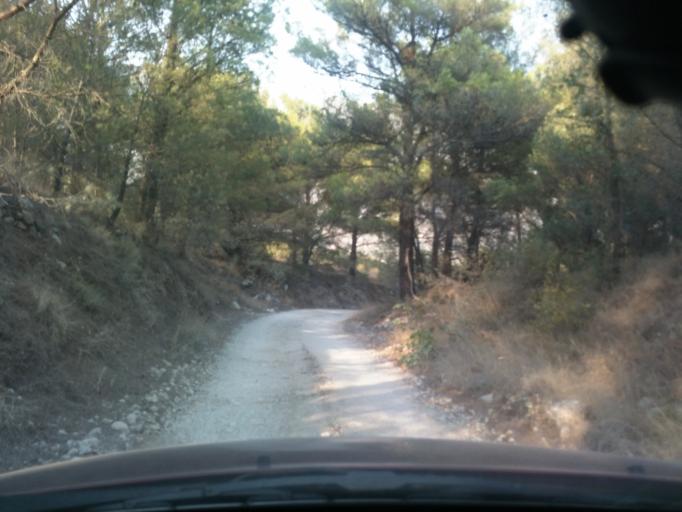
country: HR
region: Splitsko-Dalmatinska
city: Baska Voda
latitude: 43.3514
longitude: 16.9580
